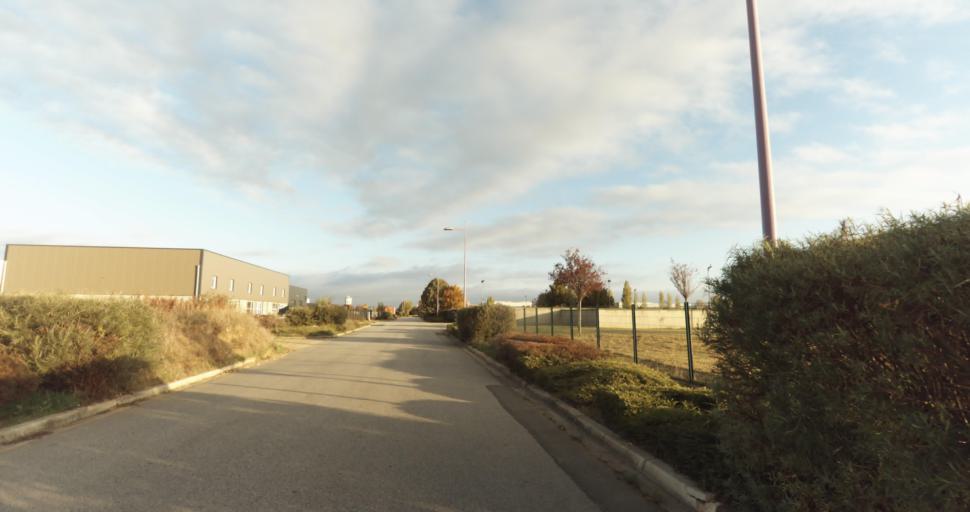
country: FR
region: Centre
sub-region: Departement d'Eure-et-Loir
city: Vernouillet
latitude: 48.7089
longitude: 1.3724
